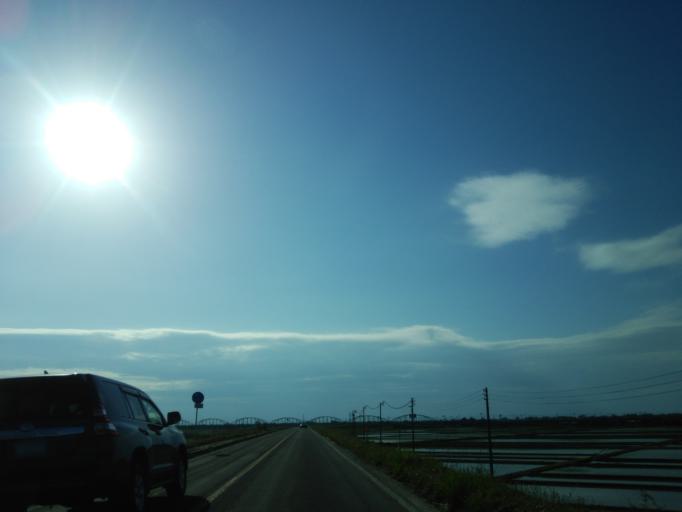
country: JP
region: Niigata
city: Niitsu-honcho
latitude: 37.8096
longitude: 139.1677
